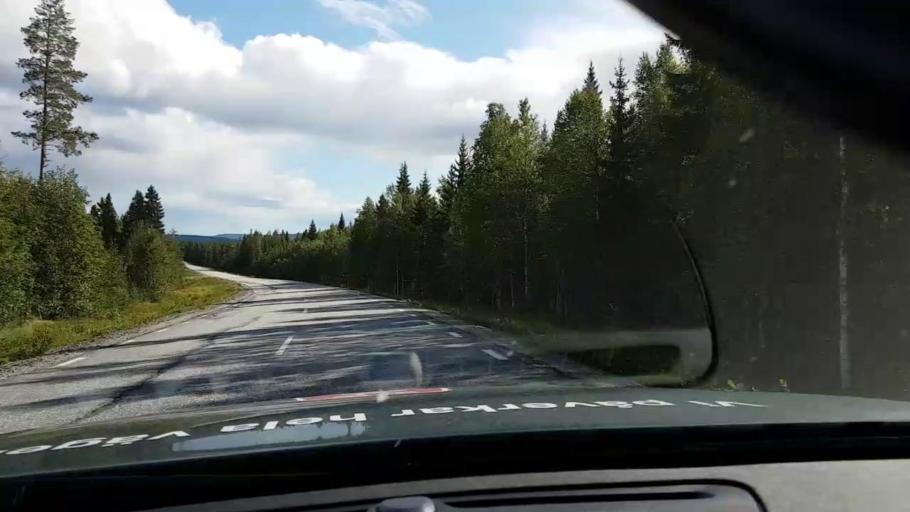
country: SE
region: Vaesternorrland
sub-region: OErnskoeldsviks Kommun
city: Bredbyn
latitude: 63.7641
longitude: 17.6871
